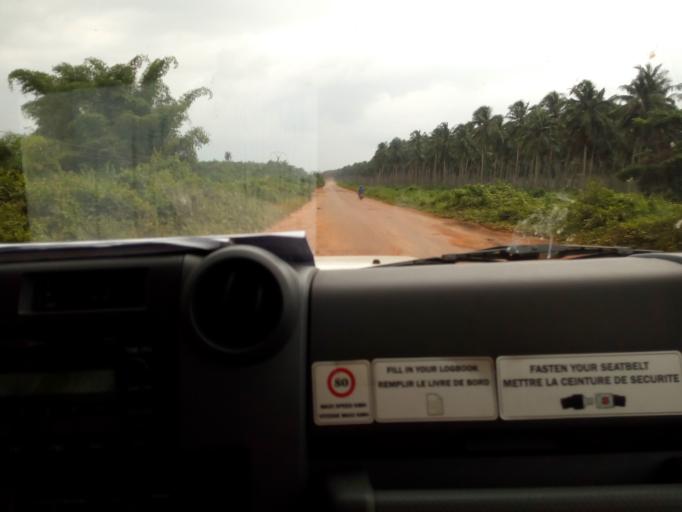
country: CI
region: Bas-Sassandra
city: Tabou
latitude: 4.5299
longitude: -7.2362
